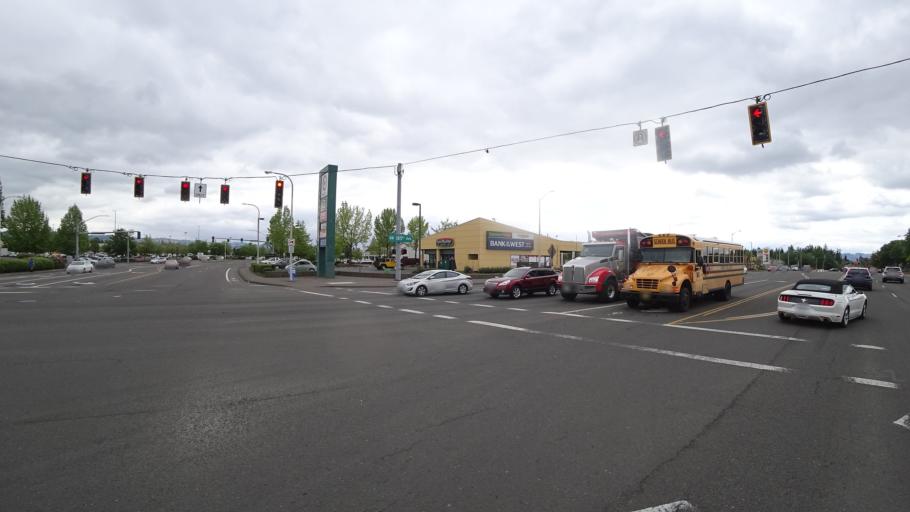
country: US
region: Oregon
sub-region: Washington County
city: Rockcreek
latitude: 45.5381
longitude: -122.8676
